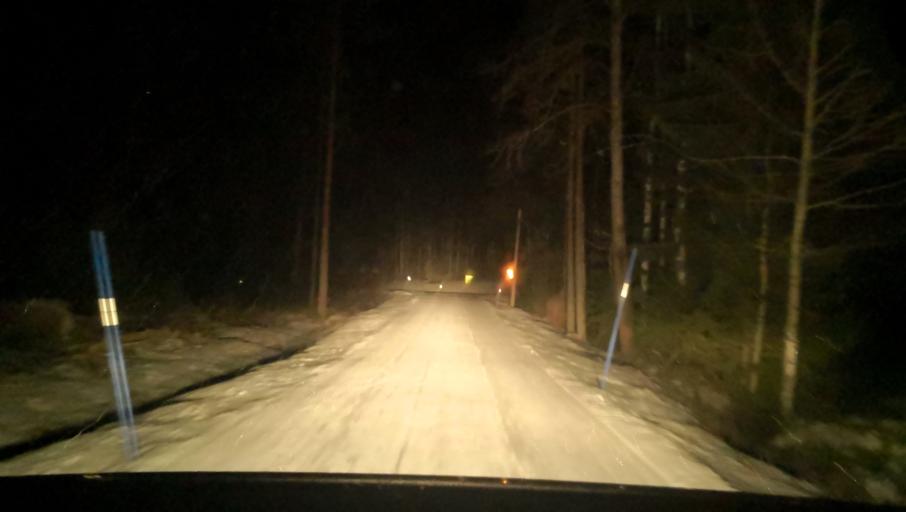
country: SE
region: Uppsala
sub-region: Heby Kommun
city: Tarnsjo
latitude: 60.0949
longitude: 16.8780
